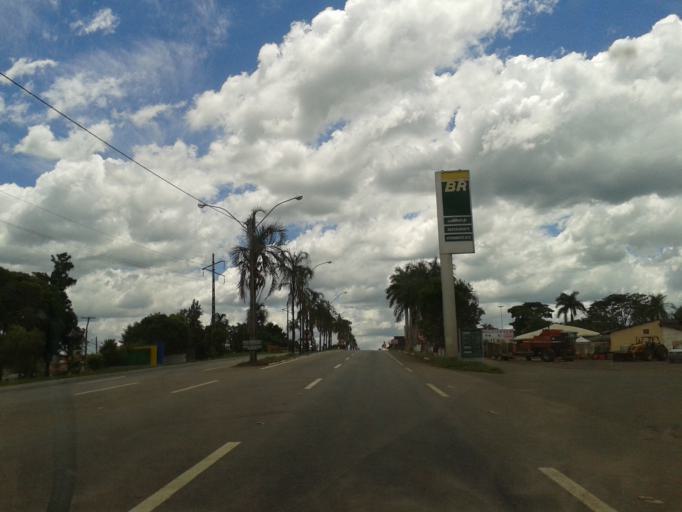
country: BR
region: Goias
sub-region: Petrolina De Goias
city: Petrolina de Goias
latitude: -16.1045
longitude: -49.3336
